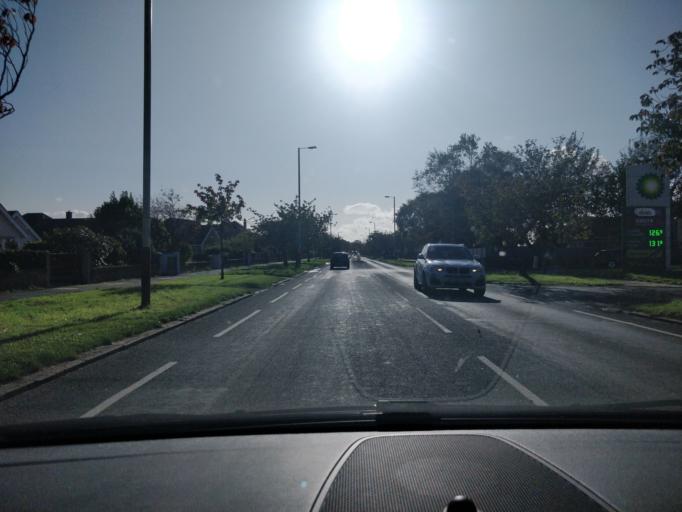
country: GB
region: England
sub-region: Lancashire
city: Banks
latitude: 53.6742
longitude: -2.9531
